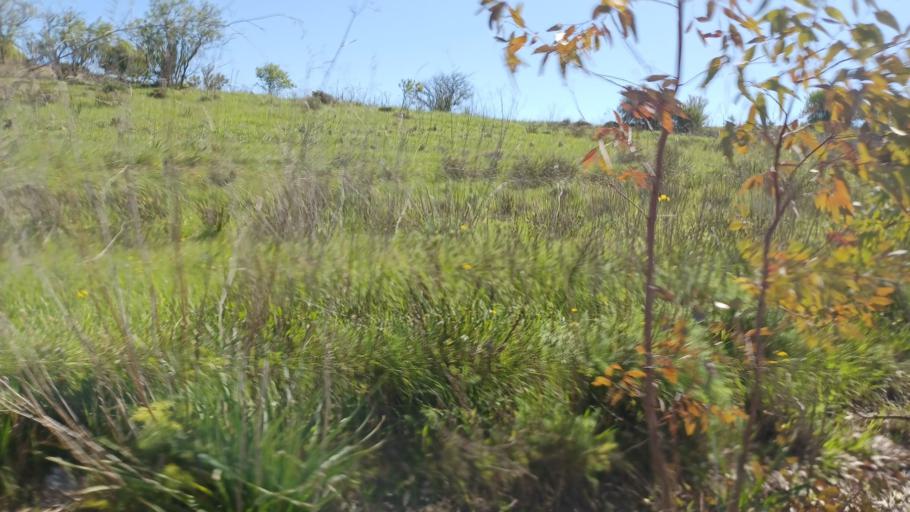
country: CY
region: Pafos
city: Polis
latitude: 34.9672
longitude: 32.3875
